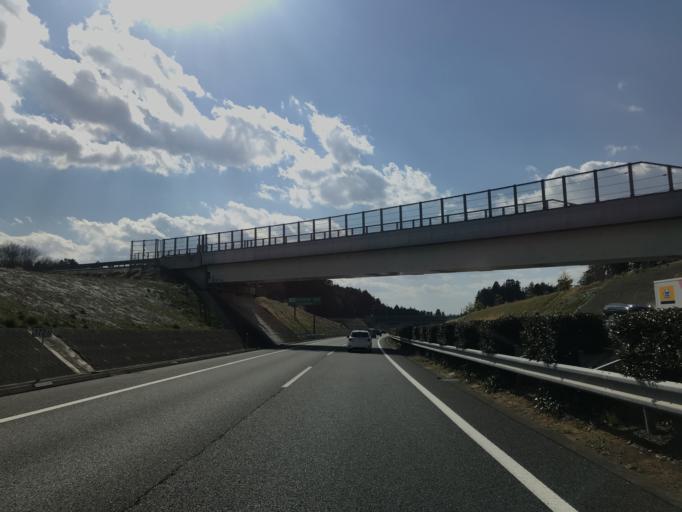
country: JP
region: Ibaraki
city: Okunoya
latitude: 36.3041
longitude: 140.4120
